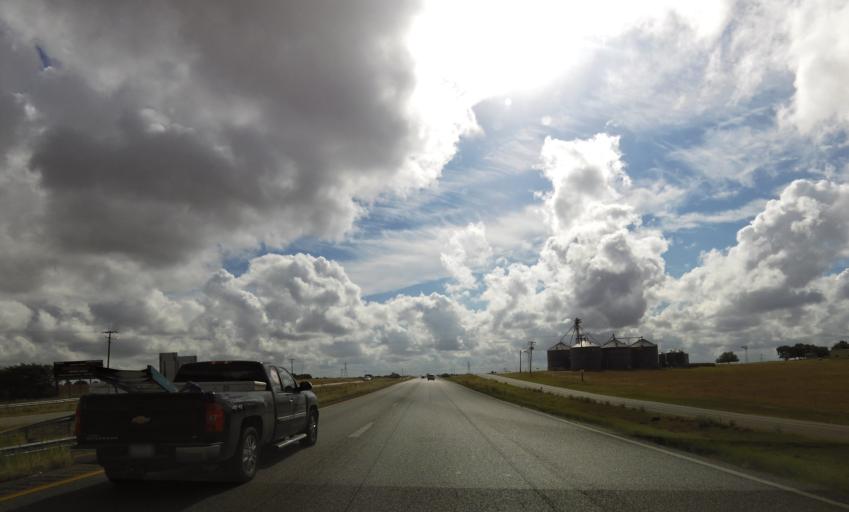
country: US
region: Texas
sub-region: Guadalupe County
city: McQueeney
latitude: 29.5414
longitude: -98.0694
